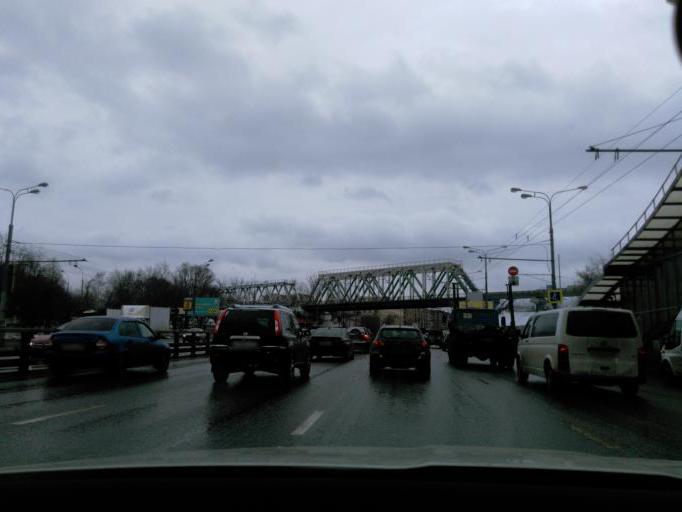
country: RU
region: Moscow
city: Likhobory
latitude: 55.8510
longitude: 37.5655
